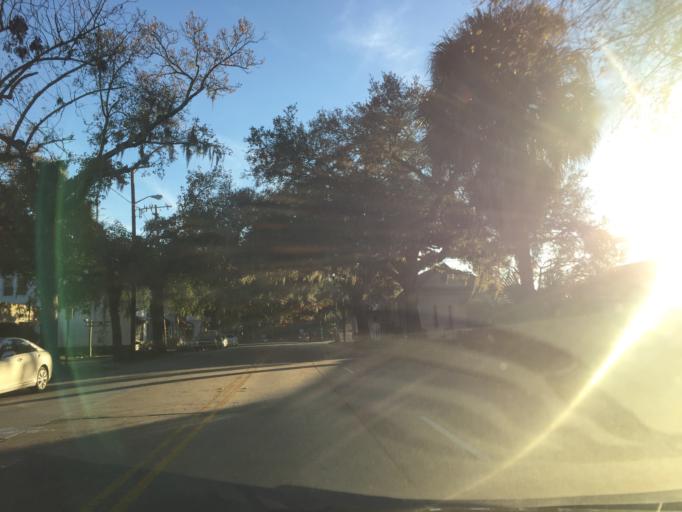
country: US
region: Georgia
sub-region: Chatham County
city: Savannah
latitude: 32.0538
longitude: -81.0989
